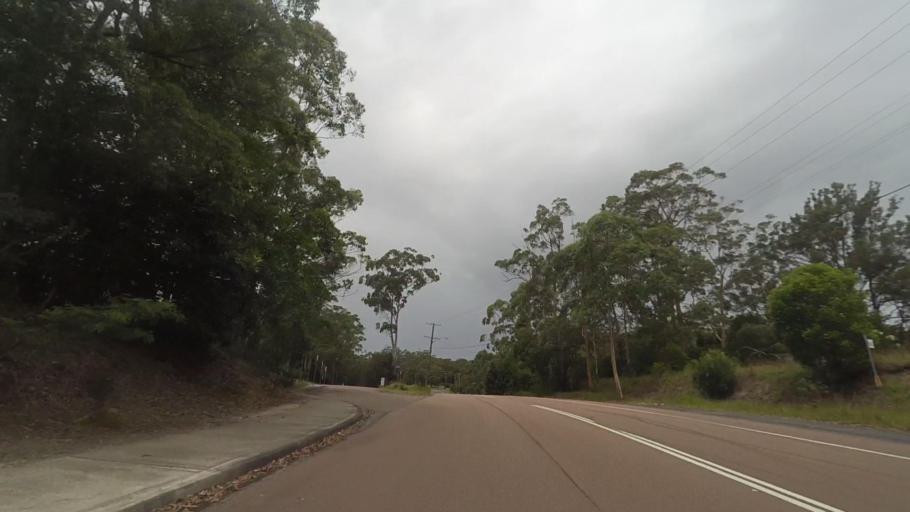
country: AU
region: New South Wales
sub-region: Wyong Shire
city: Berkeley Vale
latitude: -33.3434
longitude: 151.4239
